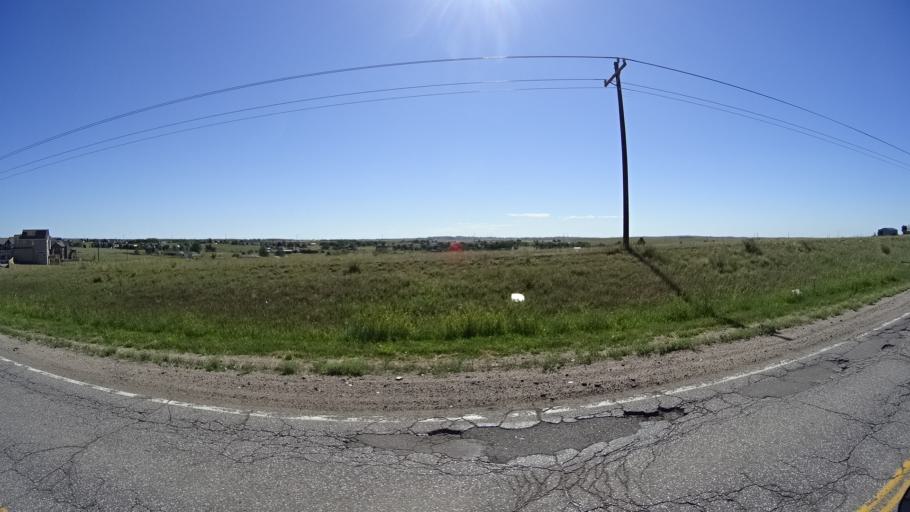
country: US
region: Colorado
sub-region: El Paso County
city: Cimarron Hills
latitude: 38.9160
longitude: -104.6832
